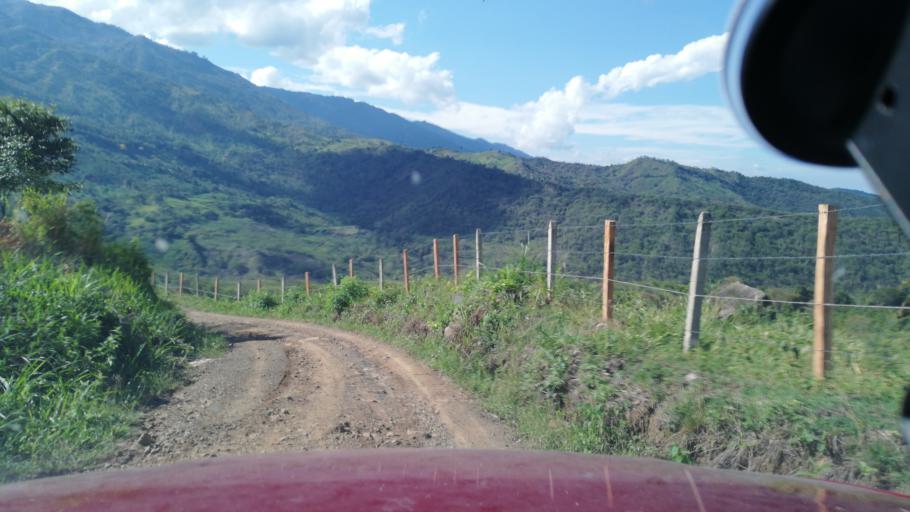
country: CO
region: Cundinamarca
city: Quipile
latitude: 4.7620
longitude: -74.6251
